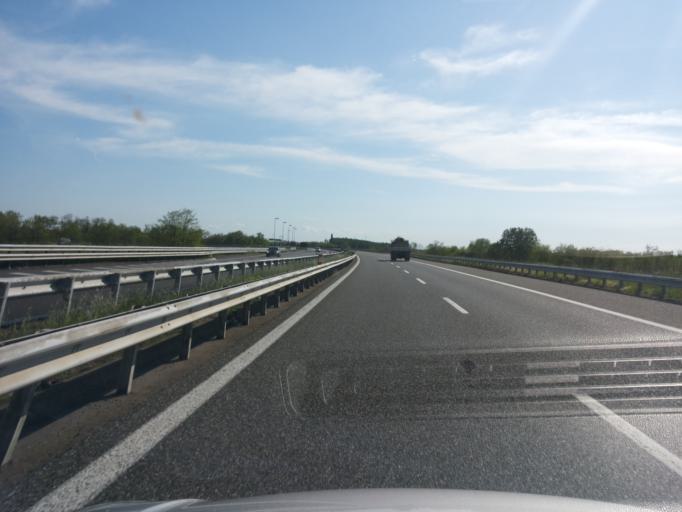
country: IT
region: Piedmont
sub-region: Provincia di Novara
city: Ghemme
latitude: 45.6094
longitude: 8.4086
